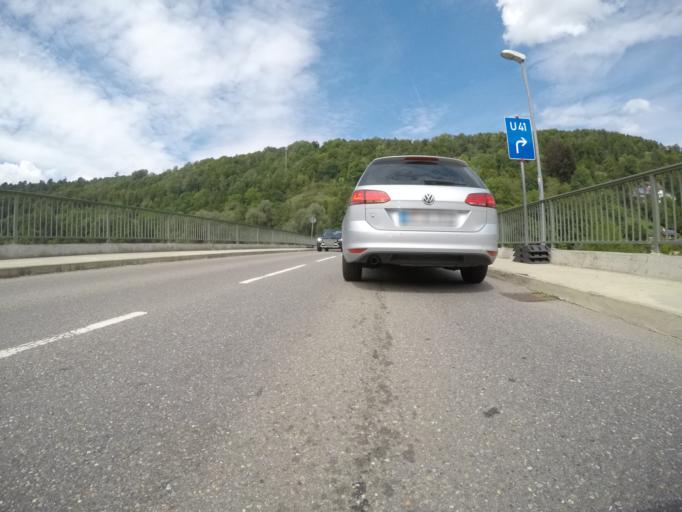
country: DE
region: Baden-Wuerttemberg
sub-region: Karlsruhe Region
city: Horb am Neckar
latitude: 48.4500
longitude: 8.7283
